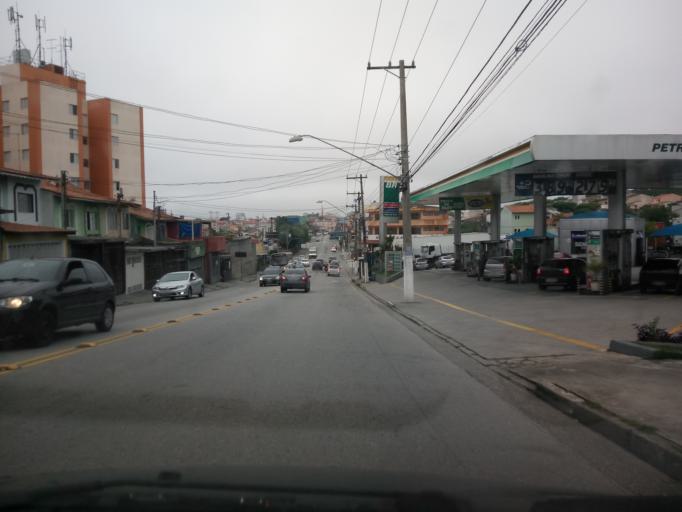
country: BR
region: Sao Paulo
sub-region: Sao Bernardo Do Campo
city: Sao Bernardo do Campo
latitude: -23.7308
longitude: -46.5686
